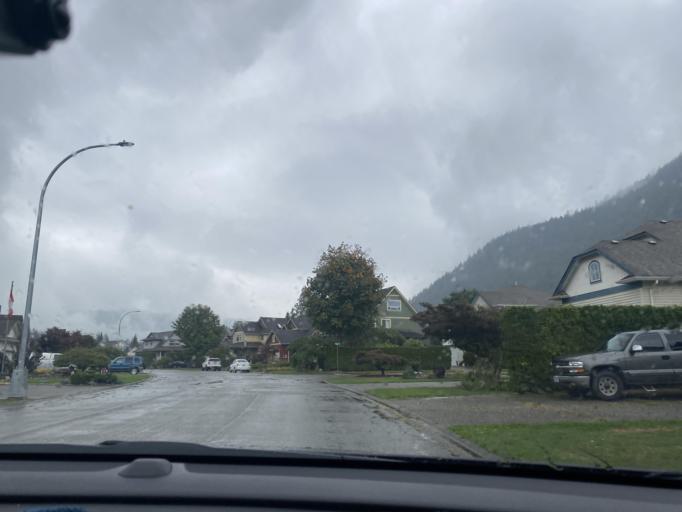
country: CA
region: British Columbia
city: Agassiz
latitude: 49.2983
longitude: -121.7809
